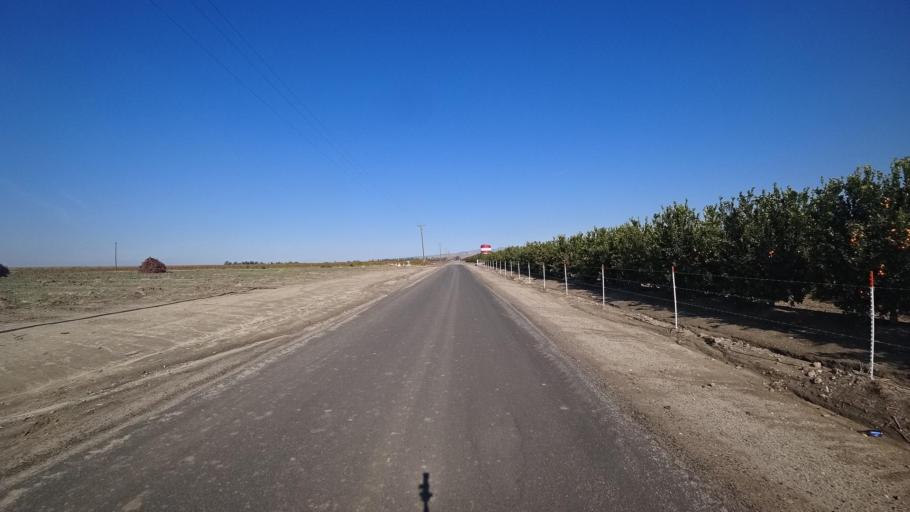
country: US
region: California
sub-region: Kern County
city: Arvin
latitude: 35.2812
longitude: -118.7708
